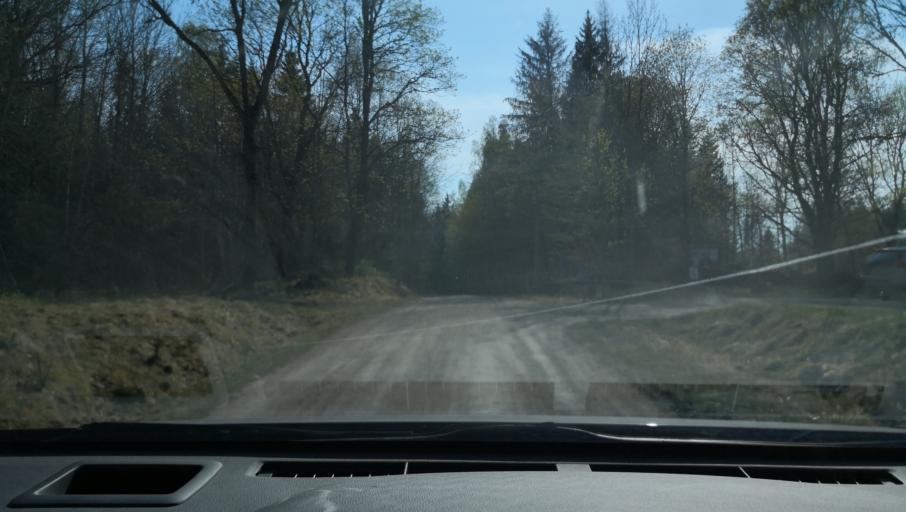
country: SE
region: Uppsala
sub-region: Heby Kommun
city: Tarnsjo
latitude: 60.2666
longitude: 16.9159
